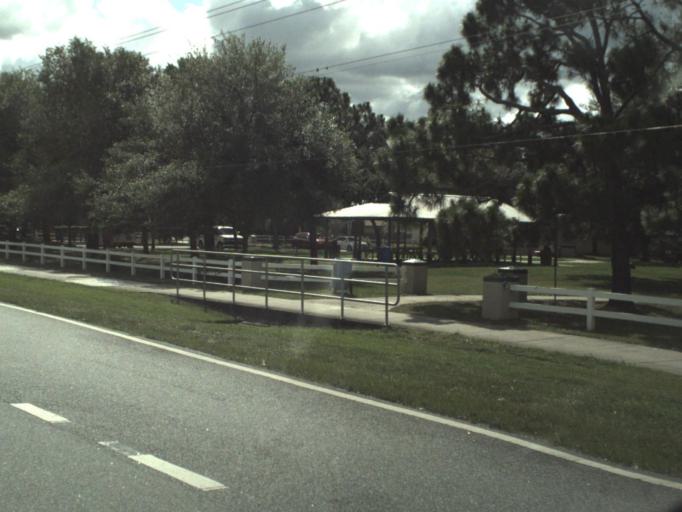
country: US
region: Florida
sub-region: Brevard County
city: Cocoa West
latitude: 28.3908
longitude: -80.7796
